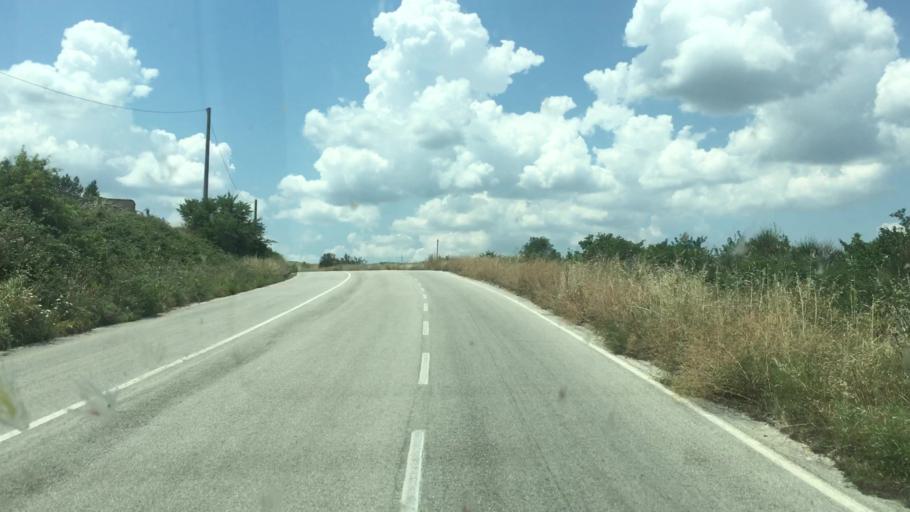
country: IT
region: Basilicate
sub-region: Provincia di Potenza
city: Tolve
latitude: 40.6990
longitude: 15.9974
